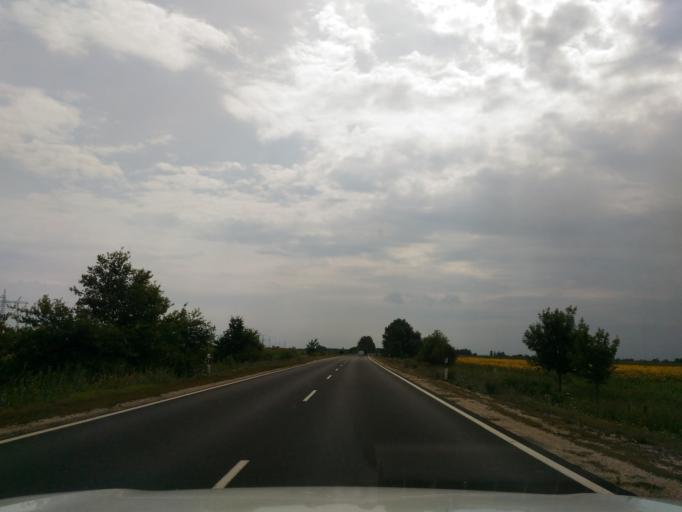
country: HU
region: Pest
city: Abony
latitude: 47.2140
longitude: 20.0528
